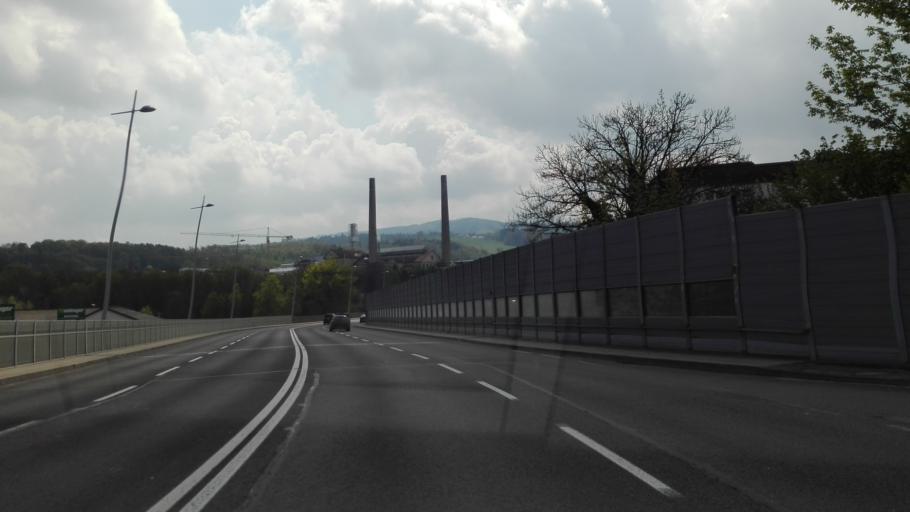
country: AT
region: Upper Austria
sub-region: Steyr Stadt
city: Steyr
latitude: 48.0451
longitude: 14.4281
